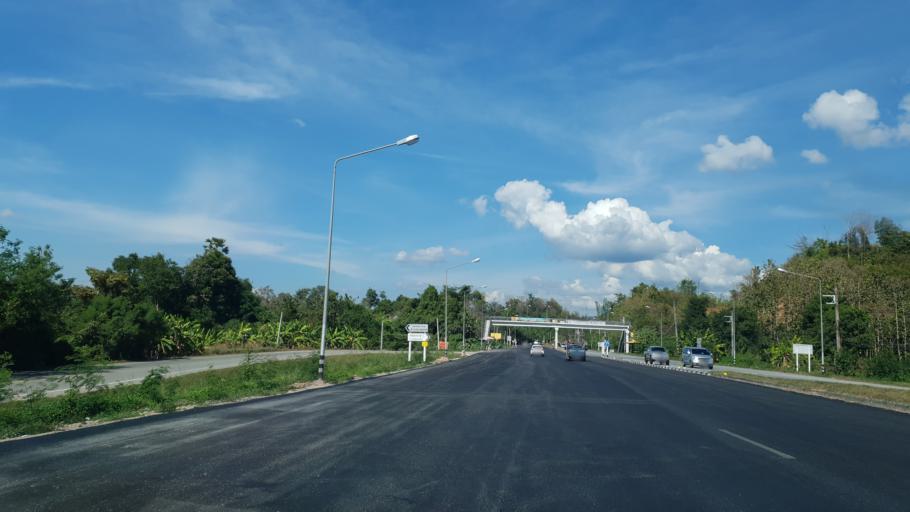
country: TH
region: Uttaradit
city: Uttaradit
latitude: 17.7336
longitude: 100.1321
